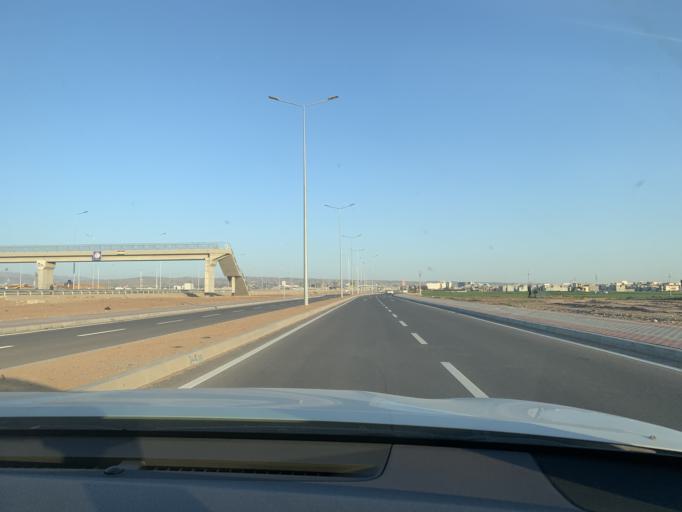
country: IQ
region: Arbil
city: Erbil
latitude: 36.2832
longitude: 44.0551
